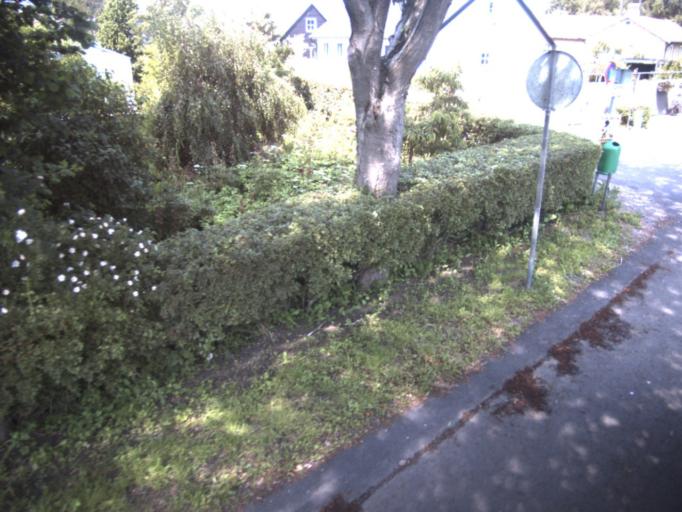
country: SE
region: Skane
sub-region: Angelholms Kommun
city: Strovelstorp
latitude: 56.1448
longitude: 12.7802
